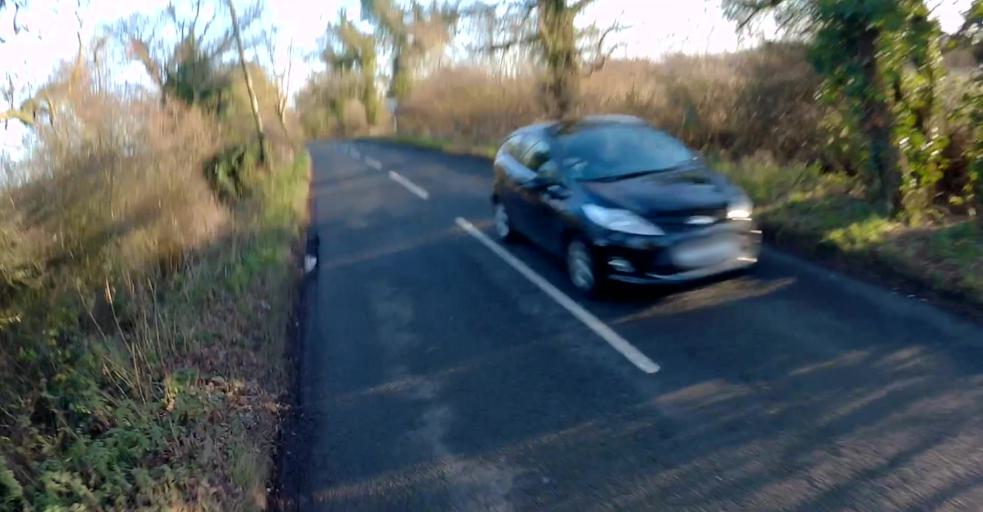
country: GB
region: England
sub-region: Hampshire
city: Old Basing
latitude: 51.2817
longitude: -1.0245
